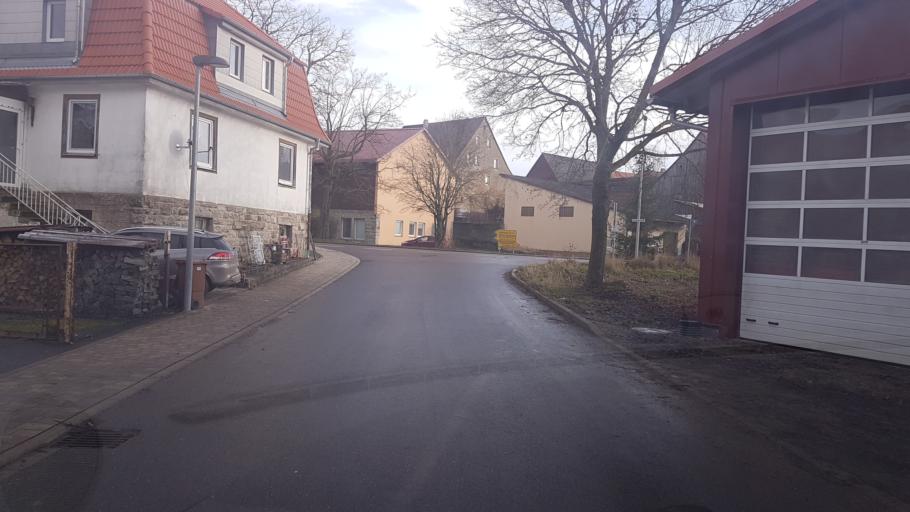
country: DE
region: Baden-Wuerttemberg
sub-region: Regierungsbezirk Stuttgart
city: Kirchberg an der Jagst
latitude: 49.2186
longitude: 10.0051
